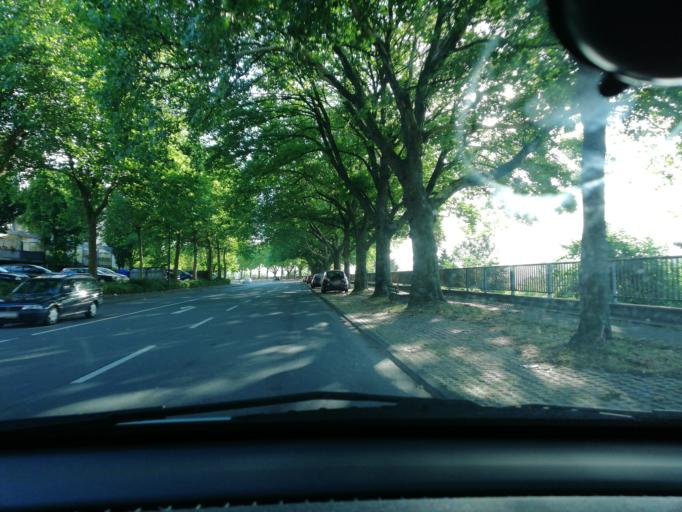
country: DE
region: North Rhine-Westphalia
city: Wulfrath
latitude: 51.2317
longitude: 7.0655
